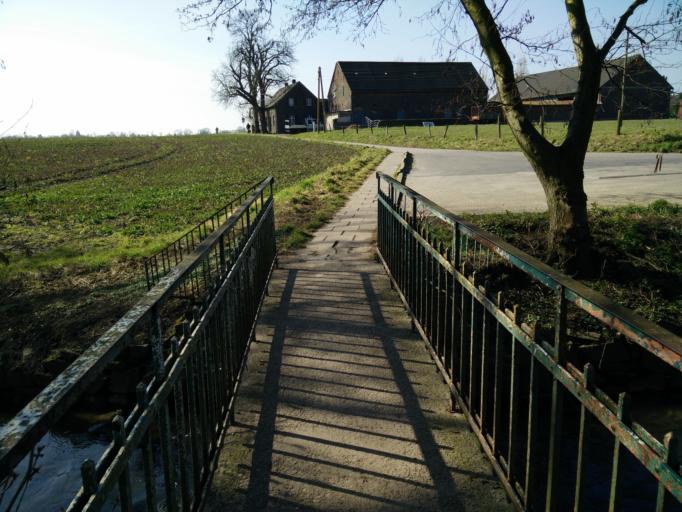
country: DE
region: North Rhine-Westphalia
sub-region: Regierungsbezirk Dusseldorf
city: Dusseldorf
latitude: 51.3125
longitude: 6.7523
